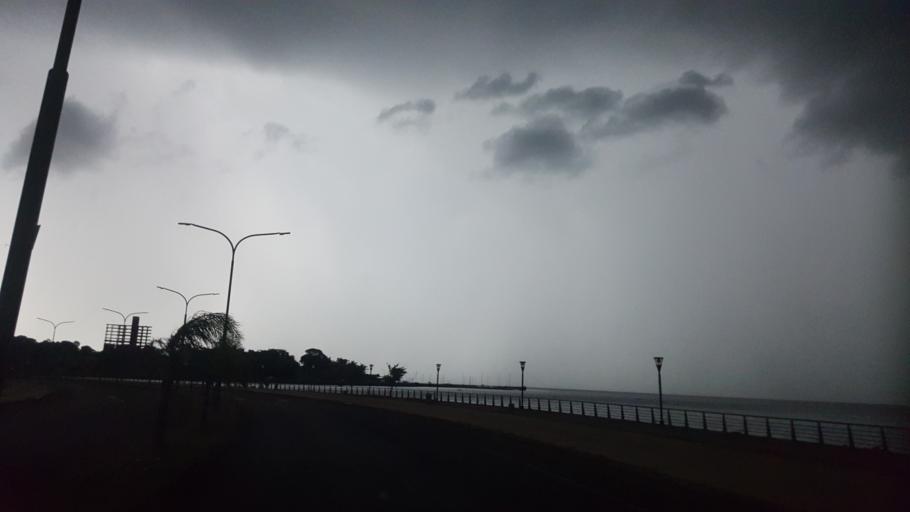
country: AR
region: Misiones
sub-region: Departamento de Capital
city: Posadas
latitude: -27.3562
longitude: -55.9060
